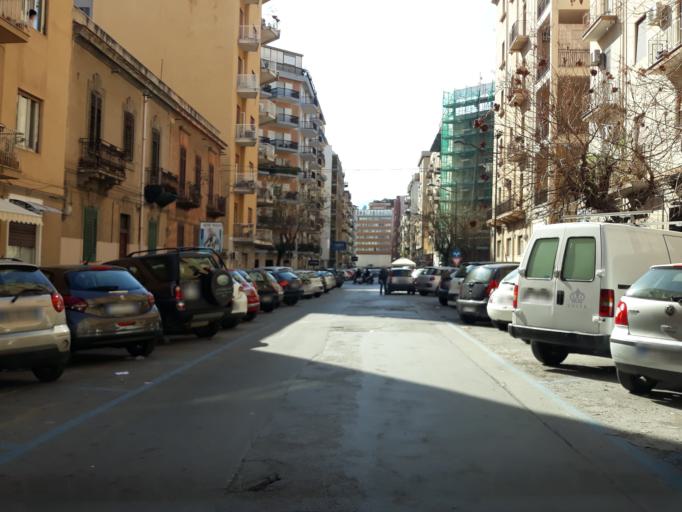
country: IT
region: Sicily
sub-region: Palermo
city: Palermo
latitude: 38.1360
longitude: 13.3463
